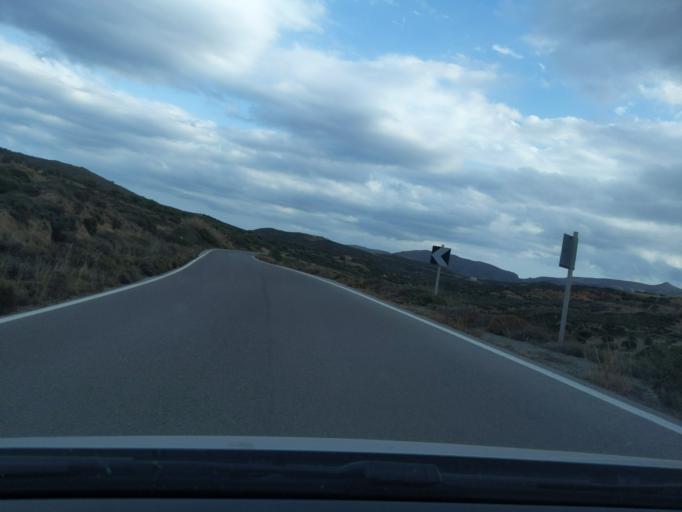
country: GR
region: Crete
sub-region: Nomos Lasithiou
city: Palekastro
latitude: 35.2310
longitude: 26.2530
